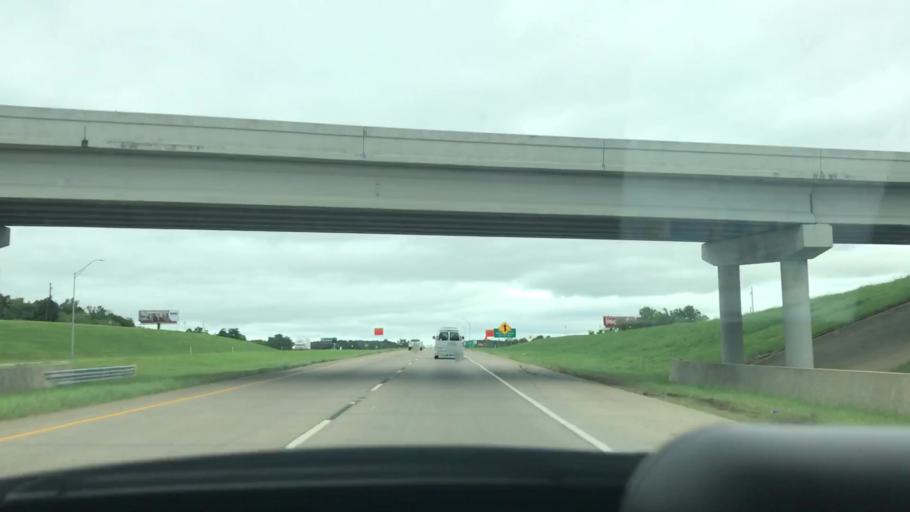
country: US
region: Texas
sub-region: Grayson County
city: Denison
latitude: 33.7209
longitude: -96.5852
